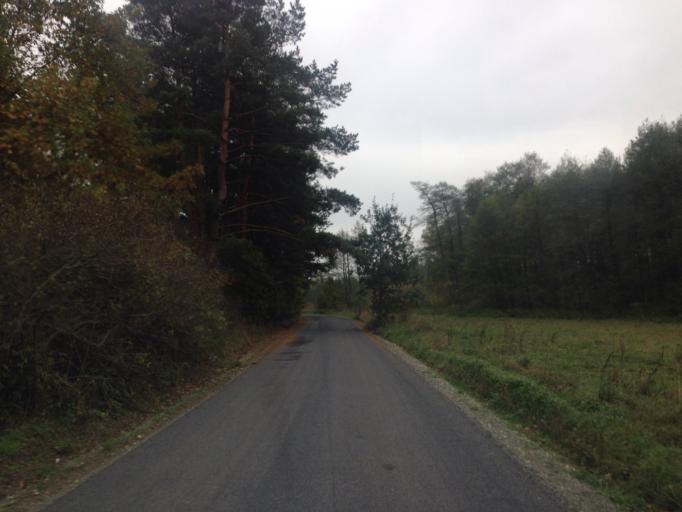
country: PL
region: Kujawsko-Pomorskie
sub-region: Powiat brodnicki
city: Bobrowo
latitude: 53.3349
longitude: 19.2237
